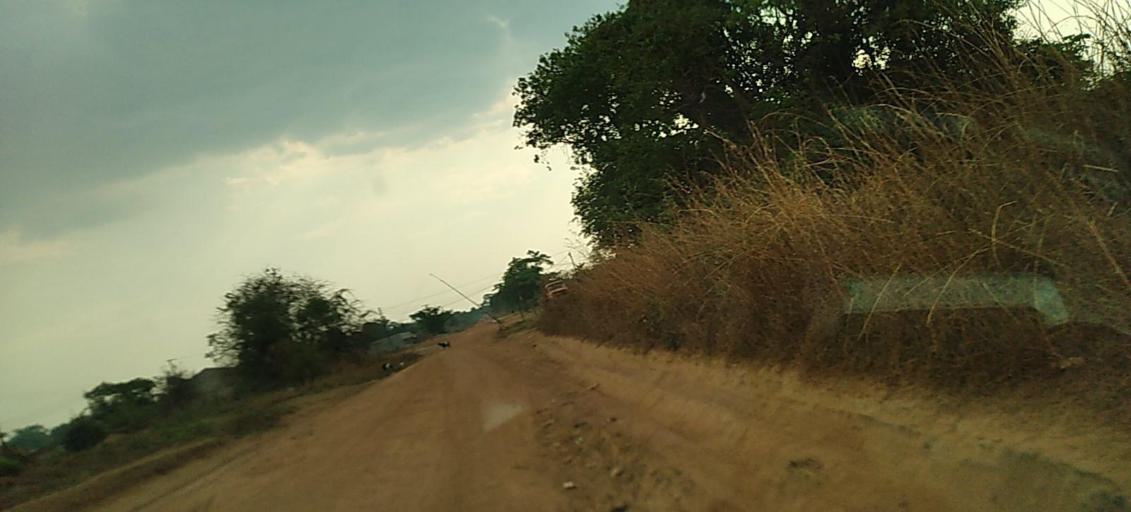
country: ZM
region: Copperbelt
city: Kalulushi
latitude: -12.9519
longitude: 27.9086
